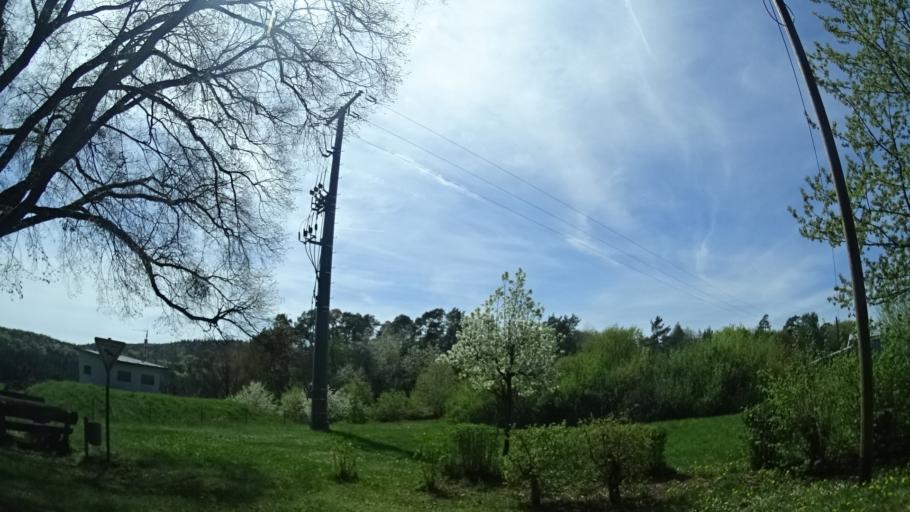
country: DE
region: Bavaria
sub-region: Regierungsbezirk Unterfranken
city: Maroldsweisach
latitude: 50.1739
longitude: 10.6310
